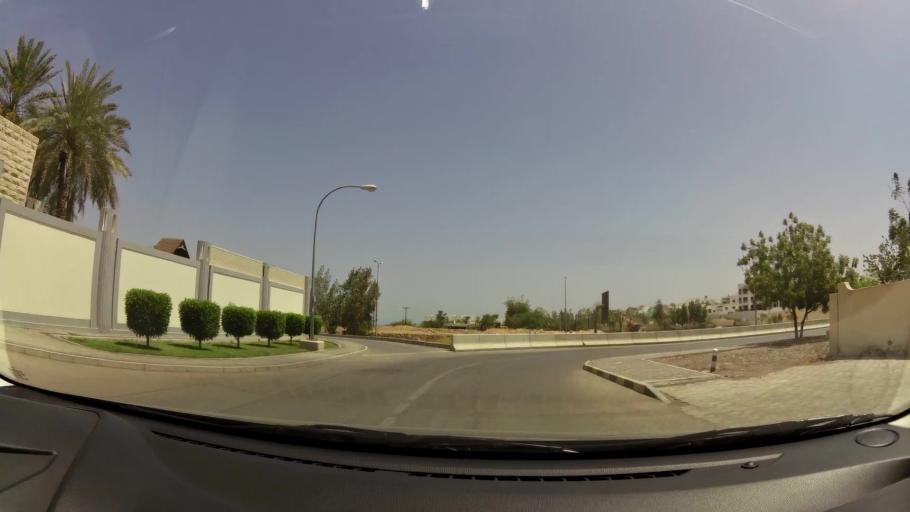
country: OM
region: Muhafazat Masqat
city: Bawshar
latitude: 23.5897
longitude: 58.4519
